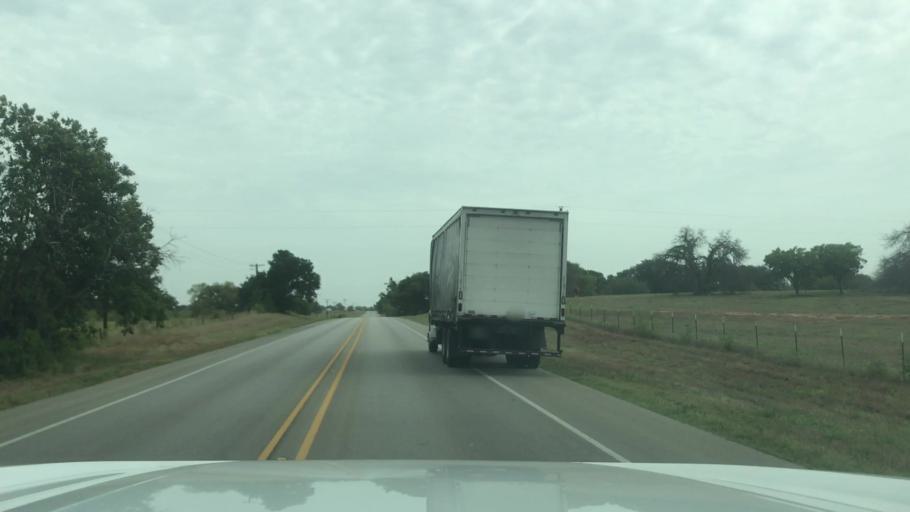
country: US
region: Texas
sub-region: Erath County
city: Dublin
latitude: 32.0904
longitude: -98.4223
